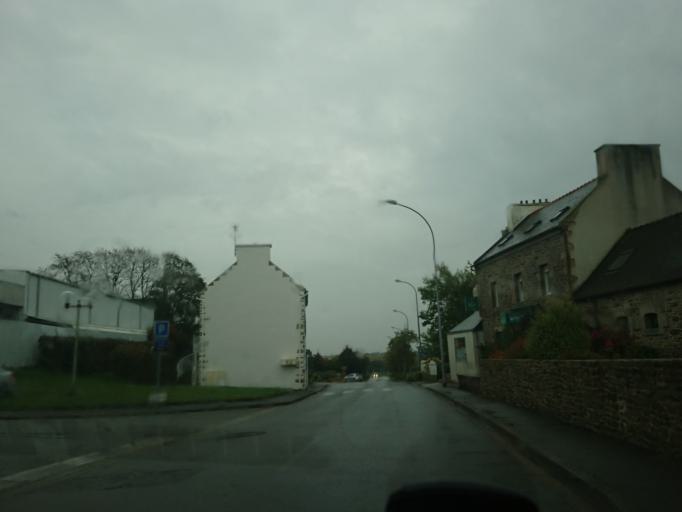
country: FR
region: Brittany
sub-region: Departement du Finistere
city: Plouguerneau
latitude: 48.6051
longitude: -4.5063
